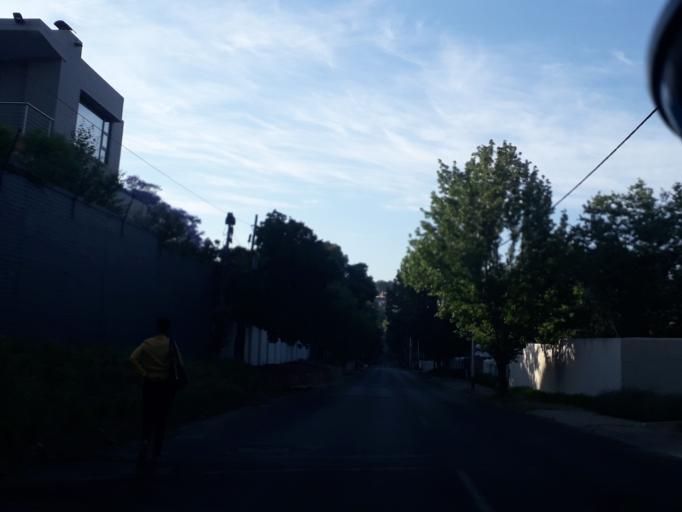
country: ZA
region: Gauteng
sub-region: City of Johannesburg Metropolitan Municipality
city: Johannesburg
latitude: -26.1171
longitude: 28.0300
